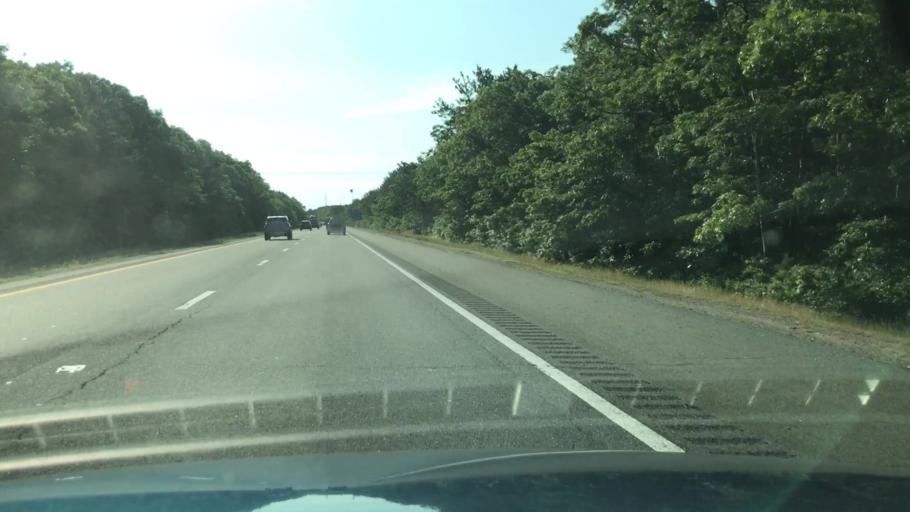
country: US
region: Massachusetts
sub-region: Barnstable County
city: Barnstable
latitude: 41.6879
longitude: -70.3054
